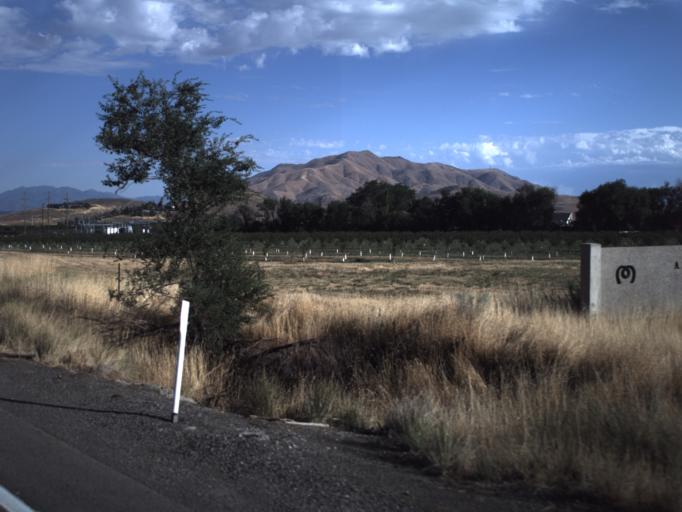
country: US
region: Utah
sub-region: Utah County
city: Santaquin
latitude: 39.9776
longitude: -111.7979
